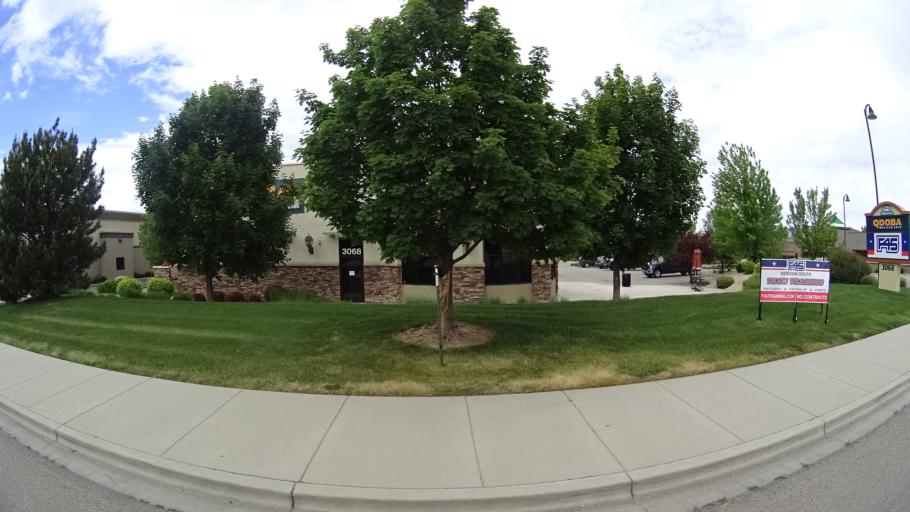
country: US
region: Idaho
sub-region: Ada County
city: Meridian
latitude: 43.5905
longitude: -116.3559
